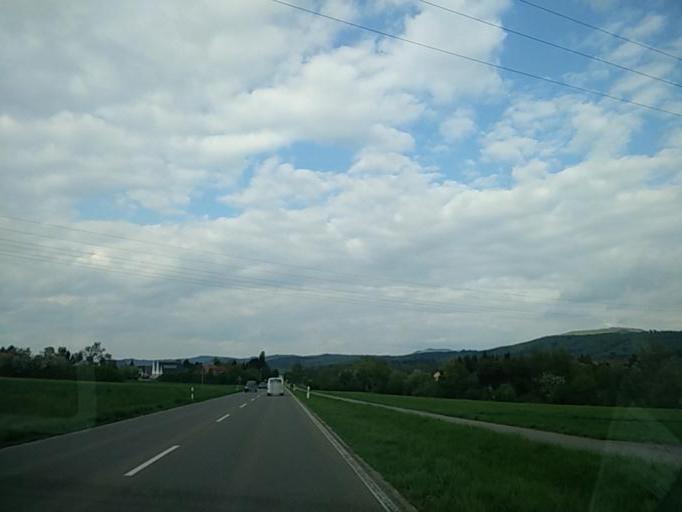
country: DE
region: Baden-Wuerttemberg
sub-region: Tuebingen Region
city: Nehren
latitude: 48.4222
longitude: 9.0589
